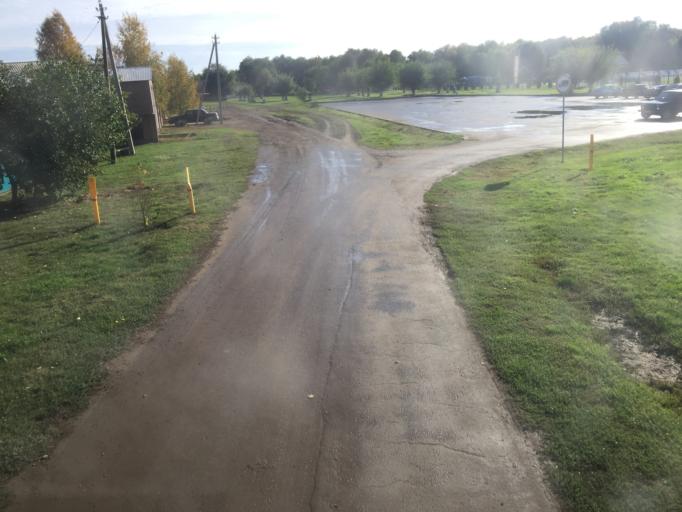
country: RU
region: Rostov
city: Peschanokopskoye
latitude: 46.1896
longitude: 41.0831
